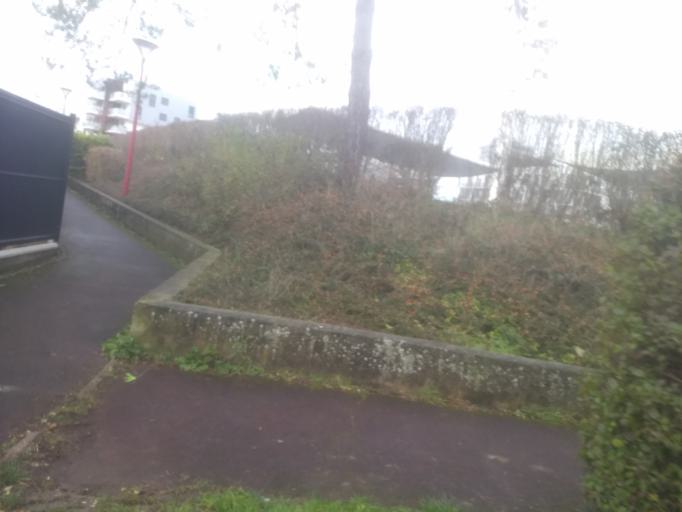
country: FR
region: Nord-Pas-de-Calais
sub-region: Departement du Pas-de-Calais
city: Saint-Nicolas
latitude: 50.3038
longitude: 2.7897
